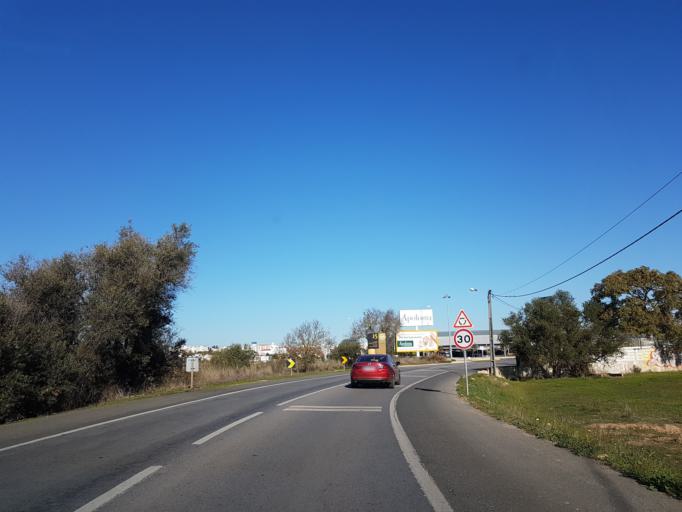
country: PT
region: Faro
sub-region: Lagoa
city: Lagoa
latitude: 37.1240
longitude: -8.4542
